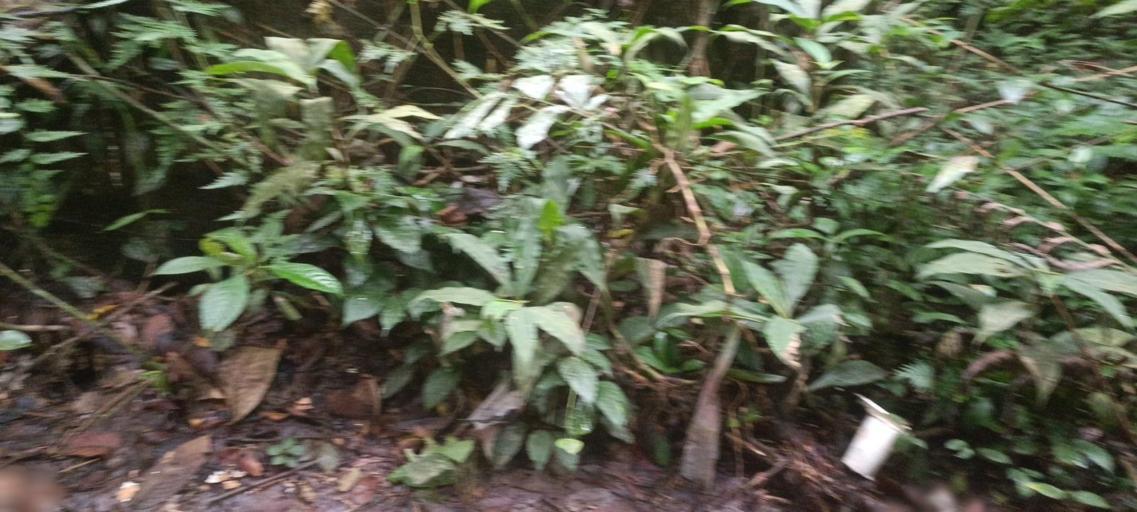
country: MY
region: Penang
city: Bukit Mertajam
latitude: 5.3683
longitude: 100.4948
